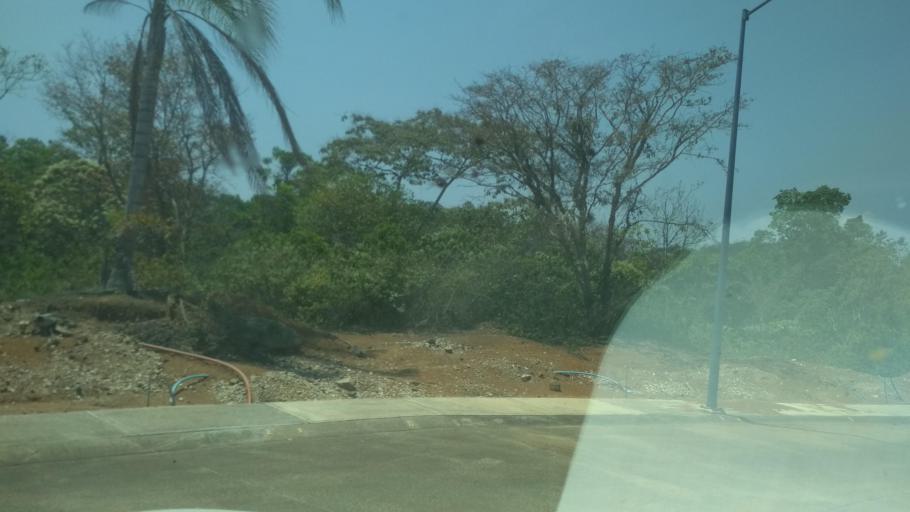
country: MX
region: Veracruz
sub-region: Emiliano Zapata
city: Las Trancas
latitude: 19.5256
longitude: -96.8743
